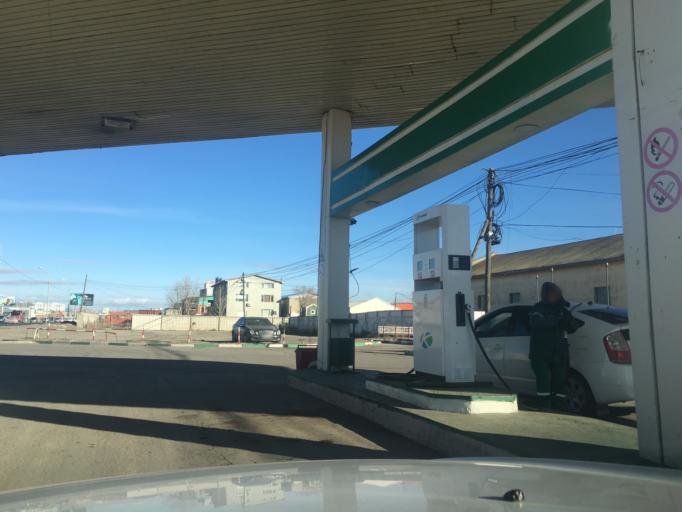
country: MN
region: Ulaanbaatar
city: Ulaanbaatar
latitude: 47.9065
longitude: 106.7779
